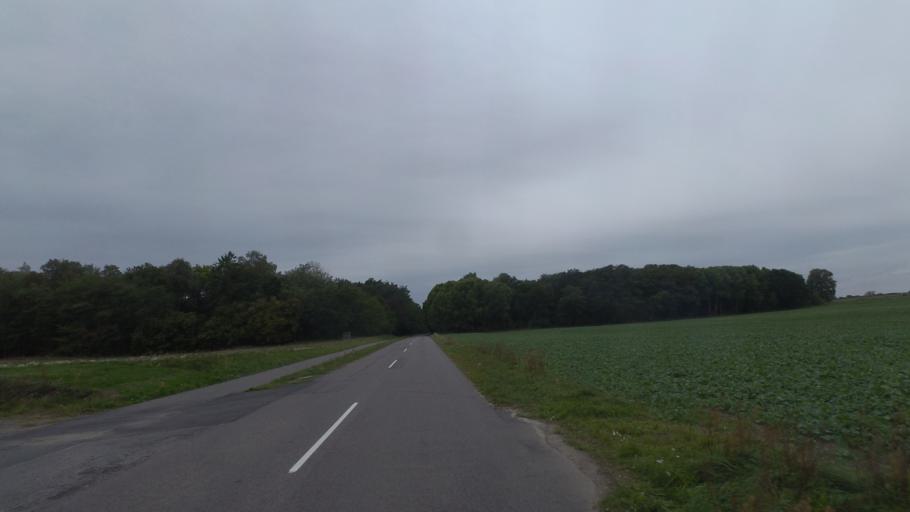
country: DK
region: Capital Region
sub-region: Bornholm Kommune
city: Nexo
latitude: 55.0024
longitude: 15.0480
